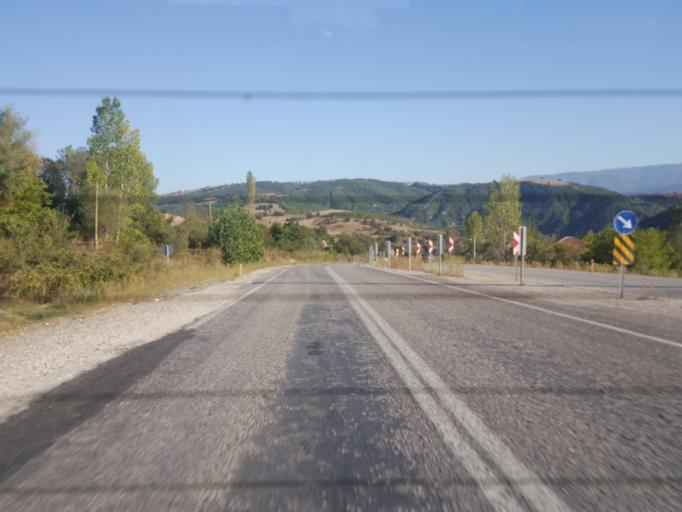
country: TR
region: Amasya
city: Tasova
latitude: 40.7635
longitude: 36.2811
